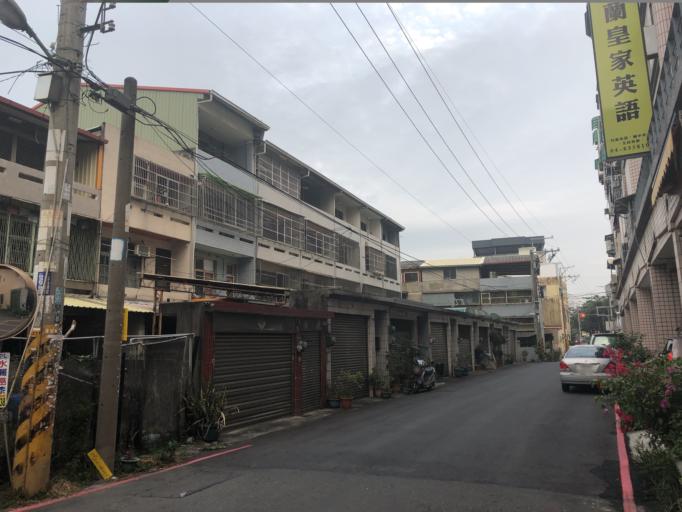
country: TW
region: Taiwan
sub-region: Changhua
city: Chang-hua
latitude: 23.9641
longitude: 120.5635
